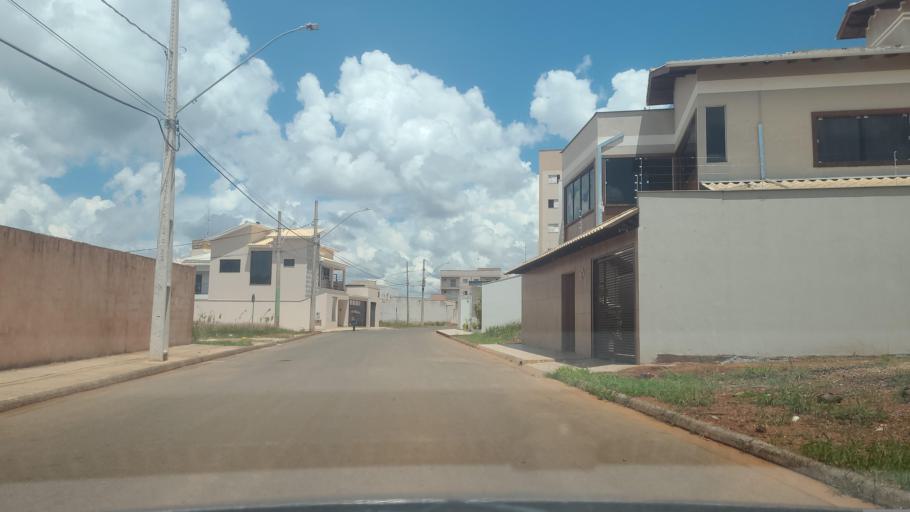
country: BR
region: Minas Gerais
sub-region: Carmo Do Paranaiba
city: Carmo do Paranaiba
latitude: -19.1999
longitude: -46.2377
